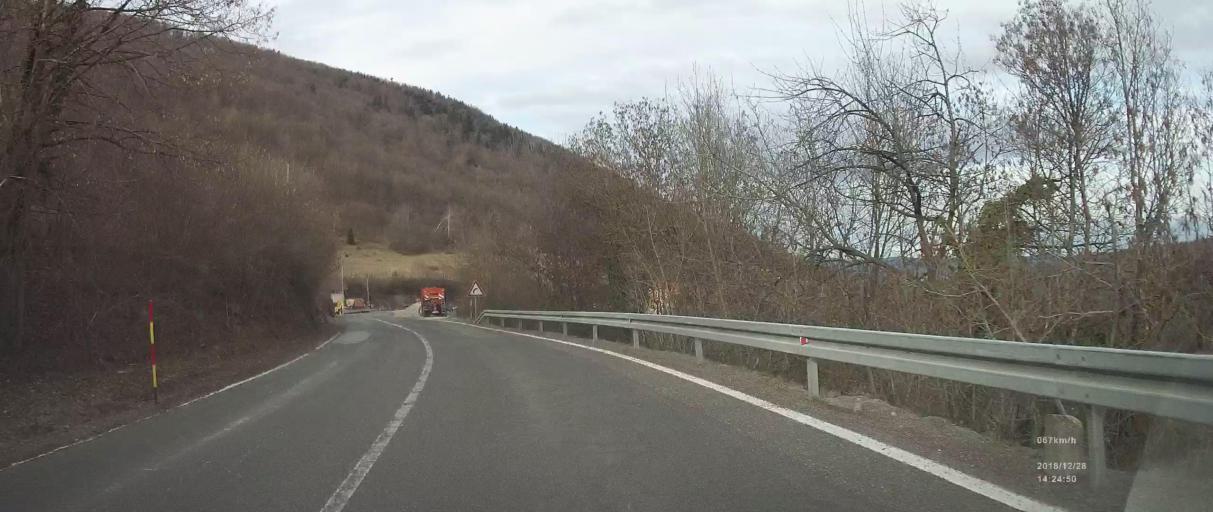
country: HR
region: Primorsko-Goranska
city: Vrbovsko
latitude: 45.3886
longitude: 15.1053
